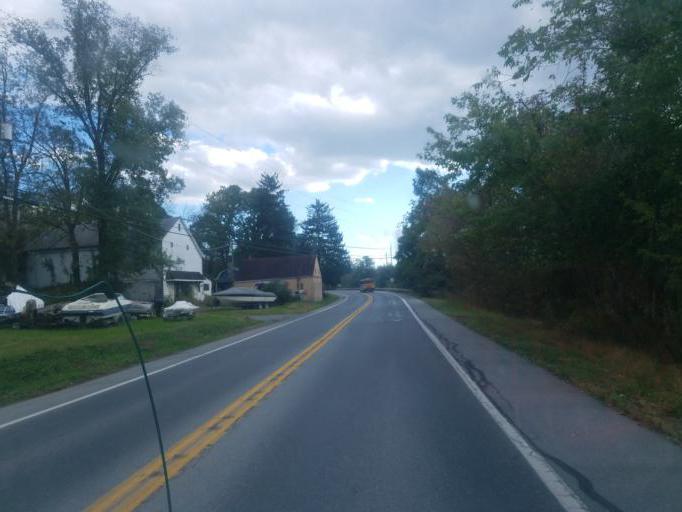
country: US
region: Pennsylvania
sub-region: Dauphin County
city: Middletown
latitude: 40.1722
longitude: -76.7235
